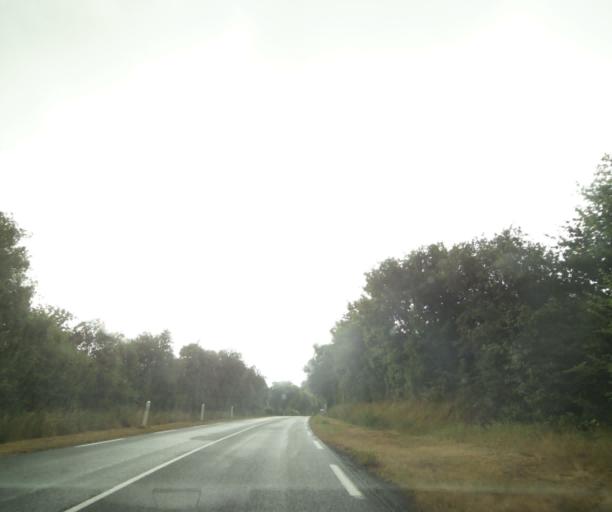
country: FR
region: Pays de la Loire
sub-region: Departement de la Vendee
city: Avrille
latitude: 46.4763
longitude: -1.5124
